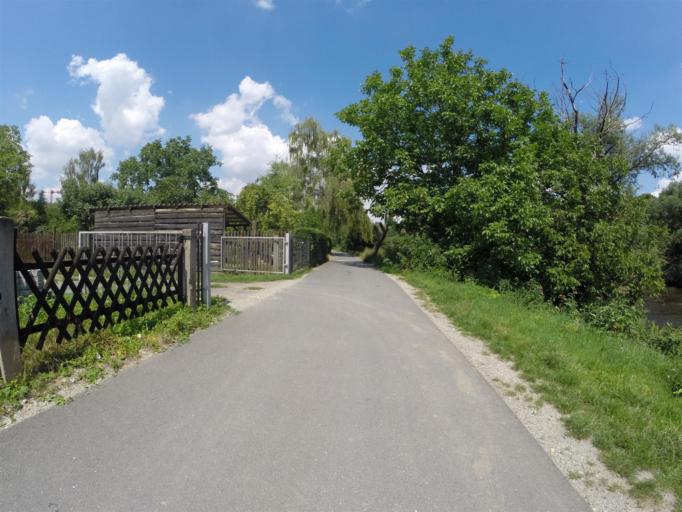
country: DE
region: Thuringia
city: Jena
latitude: 50.9299
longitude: 11.5955
